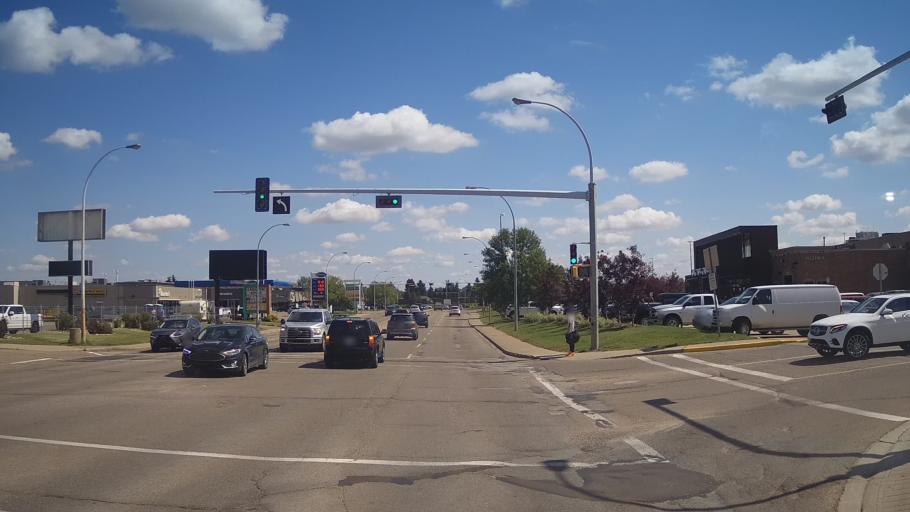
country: CA
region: Alberta
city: St. Albert
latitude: 53.5248
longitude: -113.6205
